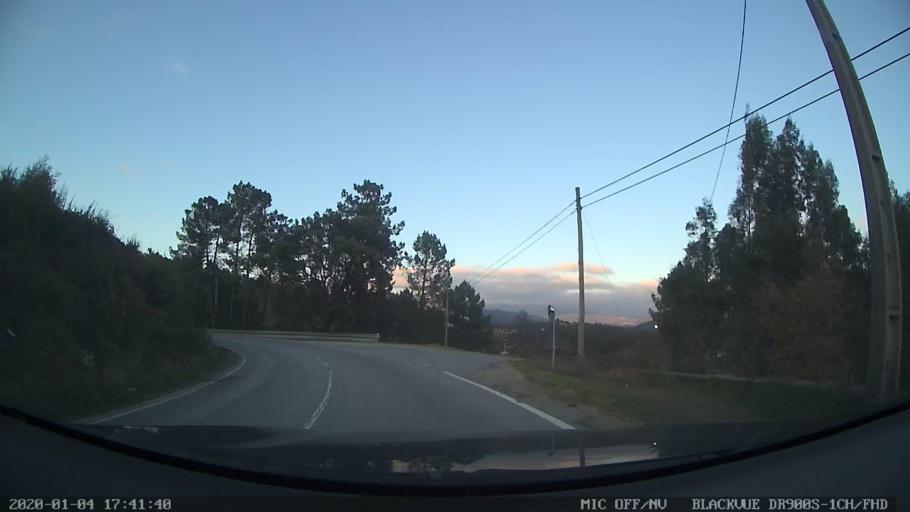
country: PT
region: Vila Real
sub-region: Mondim de Basto
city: Mondim de Basto
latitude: 41.4676
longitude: -7.9535
